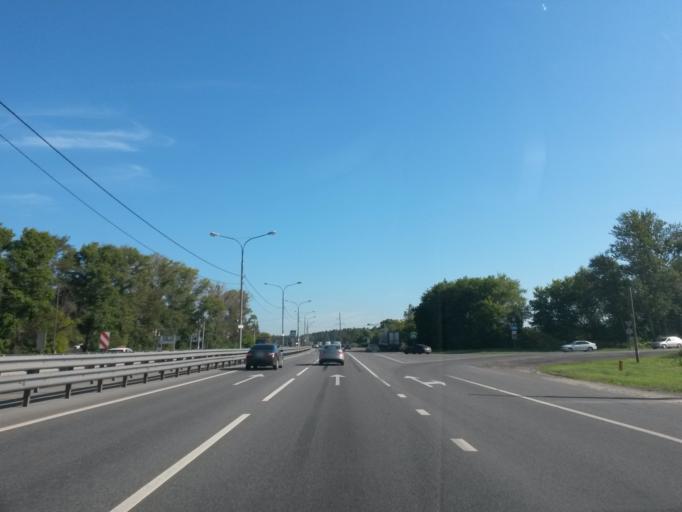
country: RU
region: Moskovskaya
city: Pushkino
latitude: 55.9977
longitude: 37.8764
